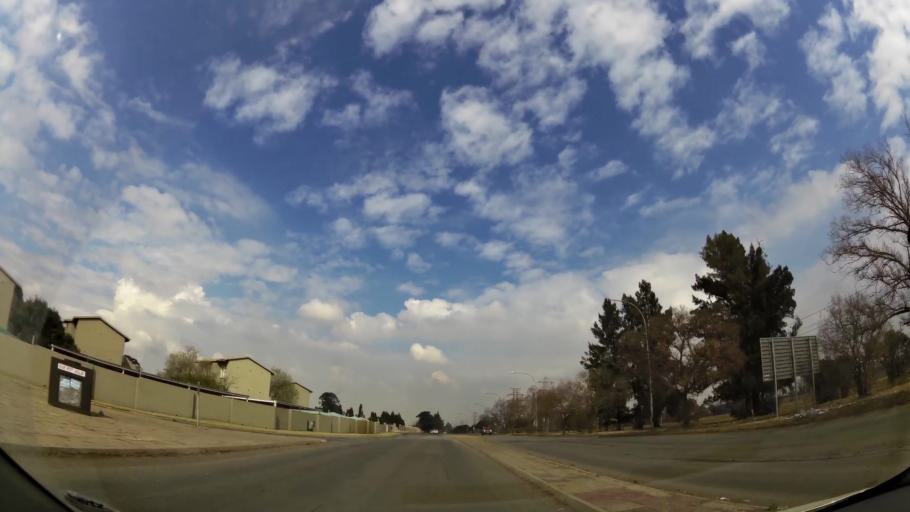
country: ZA
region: Gauteng
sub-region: Sedibeng District Municipality
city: Vereeniging
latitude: -26.6710
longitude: 27.9391
